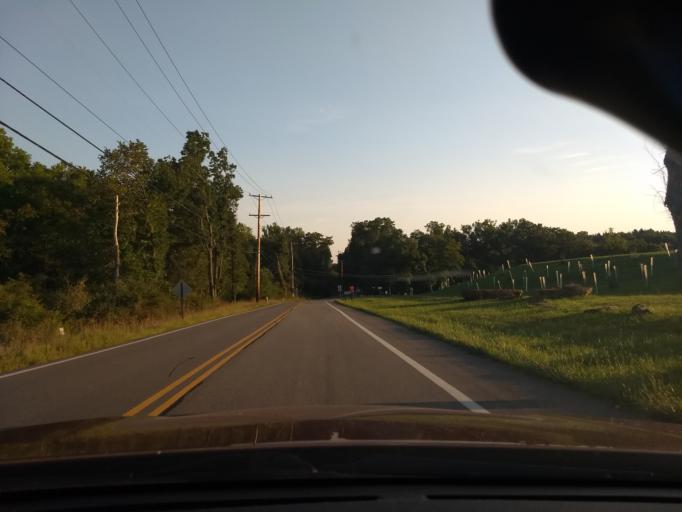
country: US
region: Pennsylvania
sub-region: Allegheny County
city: Bell Acres
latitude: 40.5913
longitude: -80.1489
